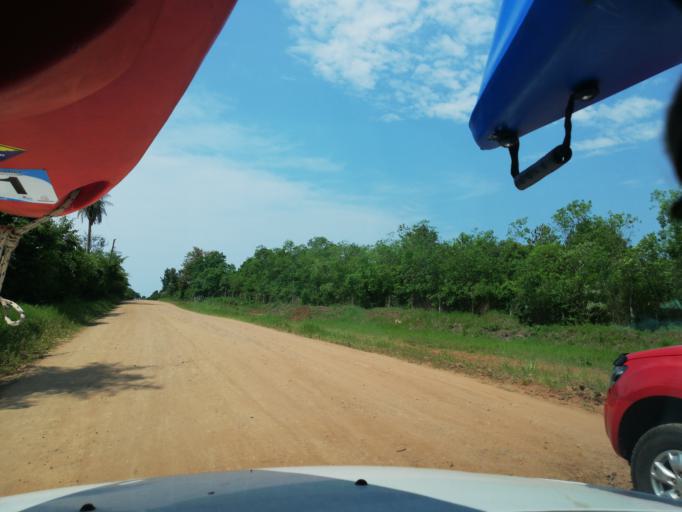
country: AR
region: Misiones
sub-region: Departamento de San Ignacio
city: San Ignacio
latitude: -27.2639
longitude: -55.5498
